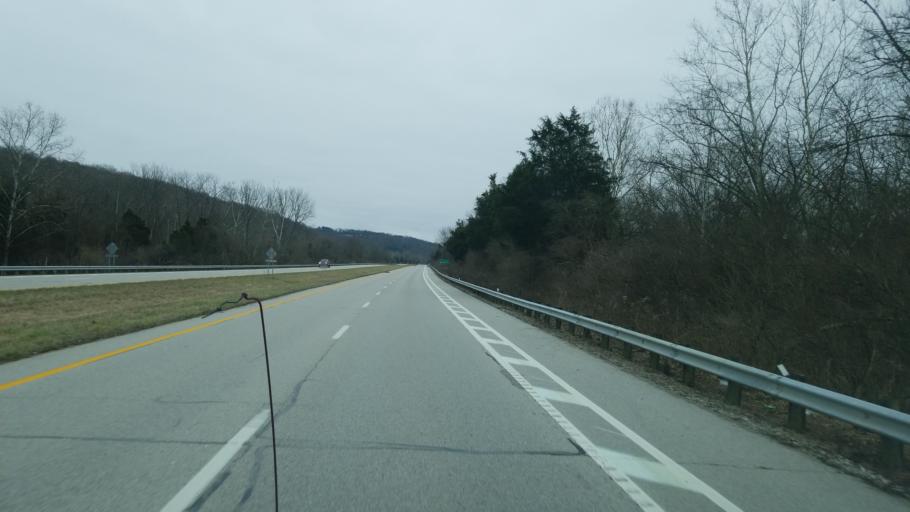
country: US
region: Ohio
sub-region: Hamilton County
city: Cherry Grove
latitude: 39.0320
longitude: -84.3308
